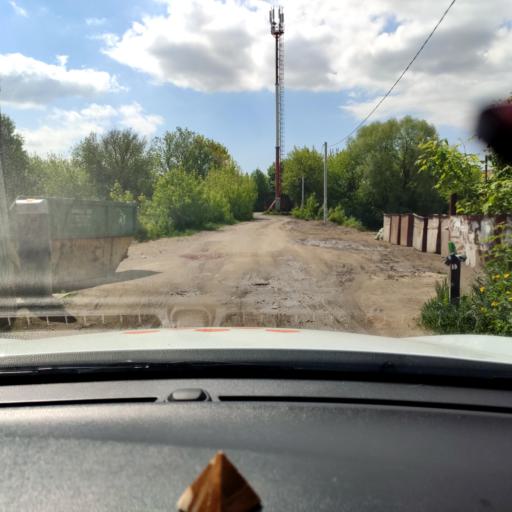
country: RU
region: Tatarstan
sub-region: Gorod Kazan'
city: Kazan
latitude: 55.8591
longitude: 49.1905
